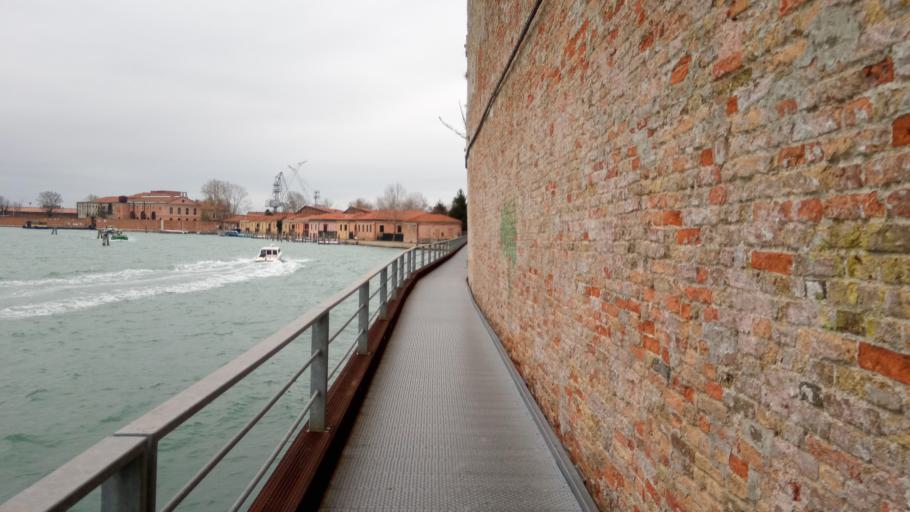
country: IT
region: Veneto
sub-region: Provincia di Venezia
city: Venice
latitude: 45.4383
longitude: 12.3527
